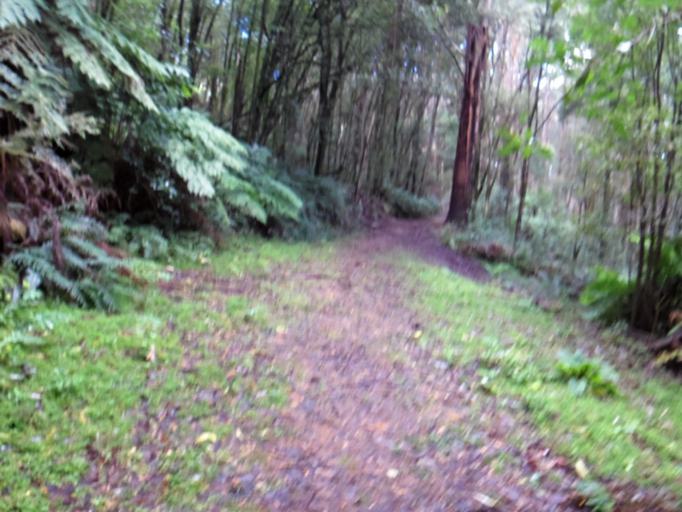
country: AU
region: Victoria
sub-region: Yarra Ranges
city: Mount Dandenong
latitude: -37.8408
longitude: 145.3498
